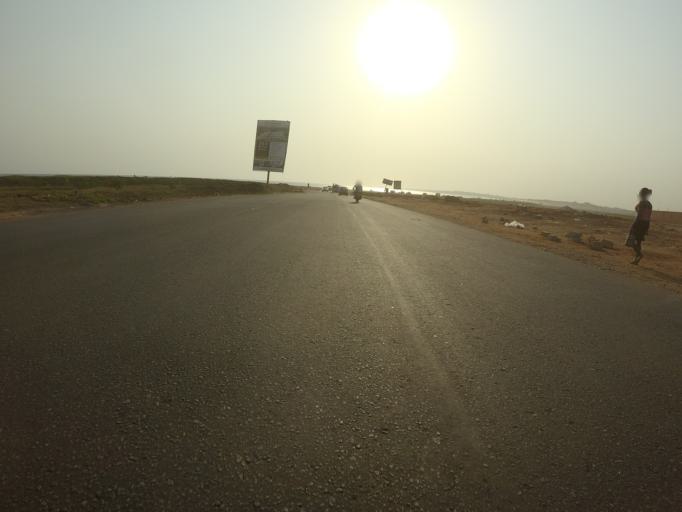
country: GH
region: Greater Accra
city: Nungua
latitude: 5.6145
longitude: -0.0277
